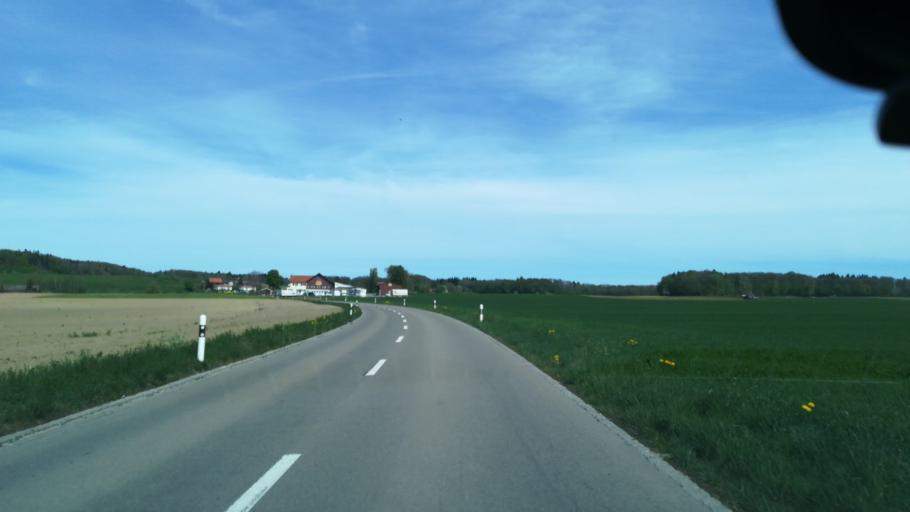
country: CH
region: Thurgau
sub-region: Weinfelden District
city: Maerstetten-Dorf
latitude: 47.6331
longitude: 9.0686
